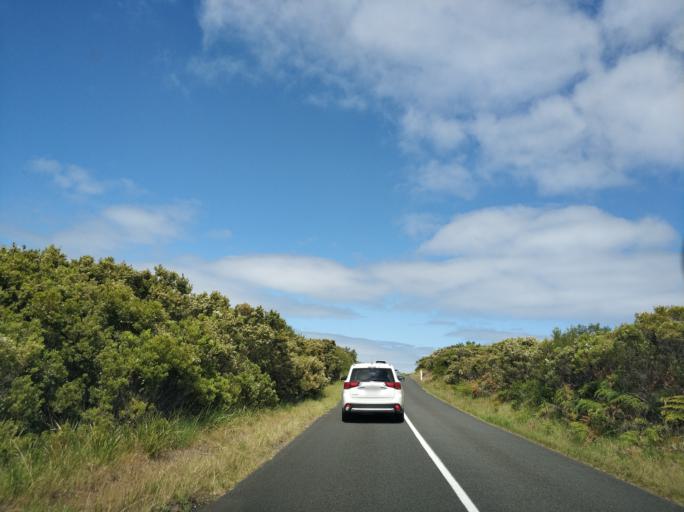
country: AU
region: Victoria
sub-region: Colac-Otway
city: Apollo Bay
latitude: -38.8519
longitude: 143.5249
